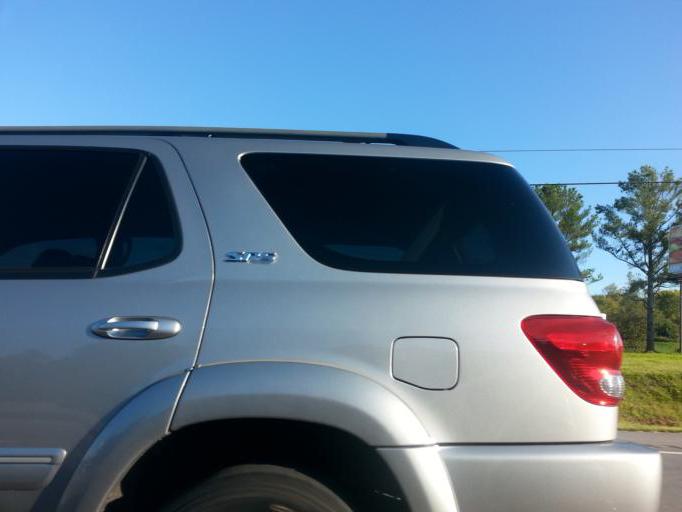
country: US
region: Alabama
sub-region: Lauderdale County
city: East Florence
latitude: 34.8323
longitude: -87.6170
